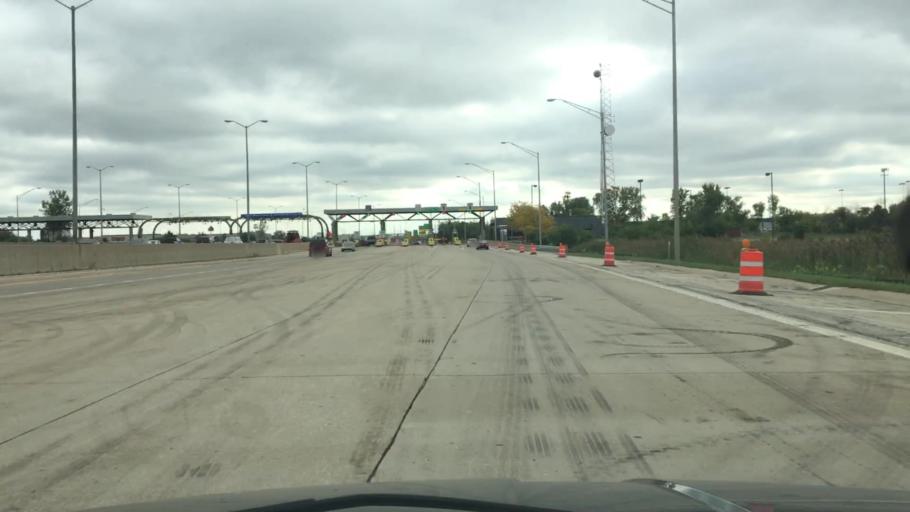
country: US
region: Illinois
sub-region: DuPage County
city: Woodridge
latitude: 41.7347
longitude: -88.0352
